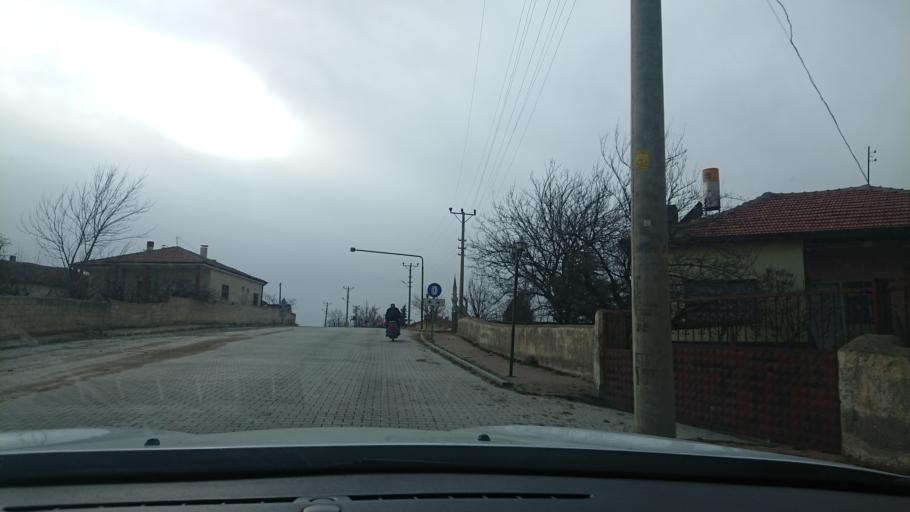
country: TR
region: Aksaray
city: Agacoren
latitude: 38.9271
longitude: 33.9556
